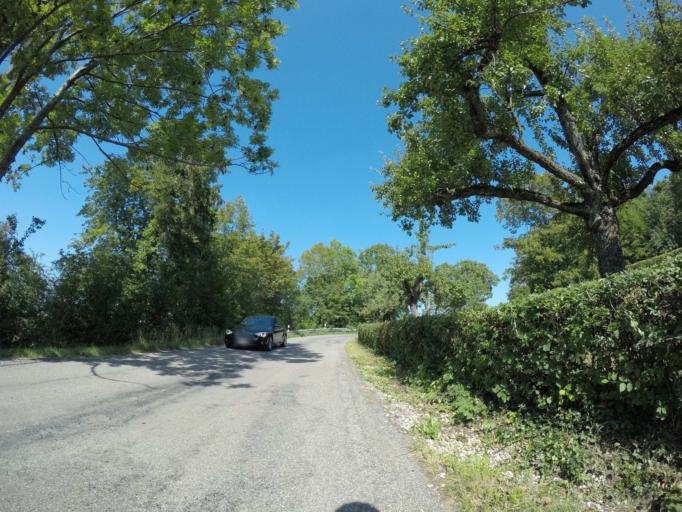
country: DE
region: Baden-Wuerttemberg
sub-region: Tuebingen Region
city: Pfullingen
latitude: 48.4682
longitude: 9.2423
